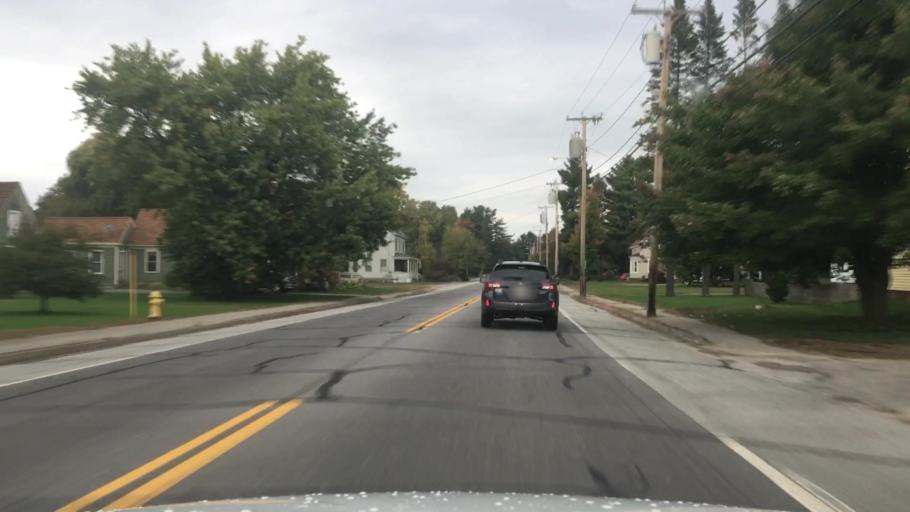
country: US
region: Maine
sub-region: York County
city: Waterboro
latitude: 43.5378
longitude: -70.7131
